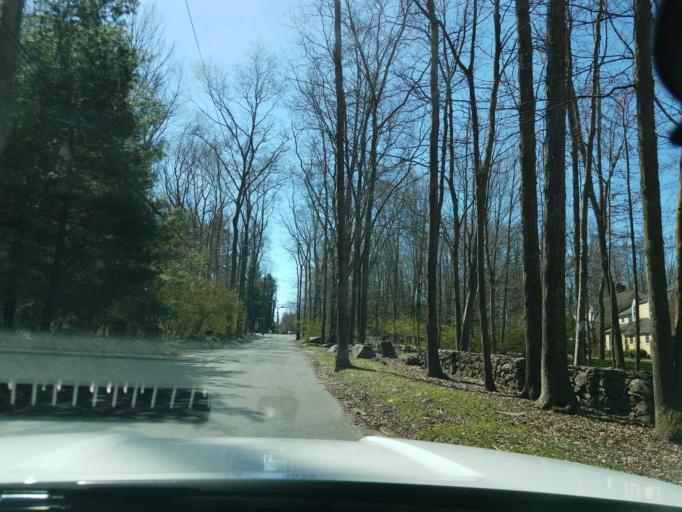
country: US
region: Connecticut
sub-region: Fairfield County
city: Wilton
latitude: 41.2198
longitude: -73.3797
